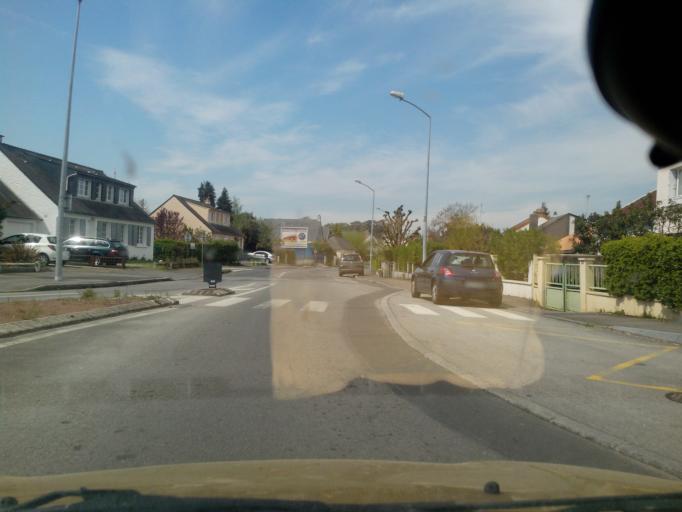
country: FR
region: Pays de la Loire
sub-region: Departement de la Loire-Atlantique
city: Orvault
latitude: 47.2500
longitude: -1.5870
